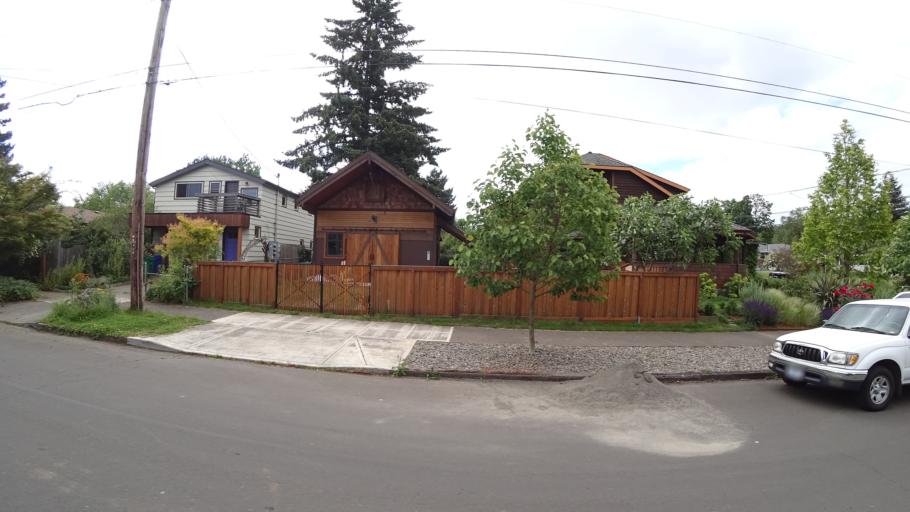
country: US
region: Oregon
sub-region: Washington County
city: West Haven
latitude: 45.5958
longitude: -122.7625
